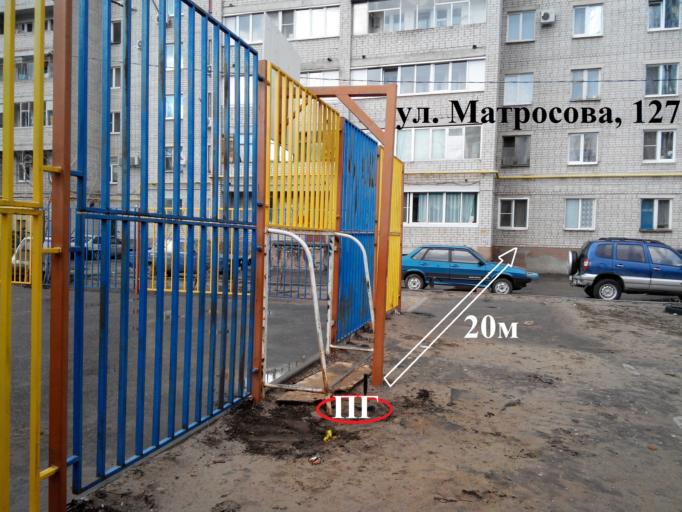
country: RU
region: Voronezj
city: Voronezh
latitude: 51.6395
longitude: 39.1607
